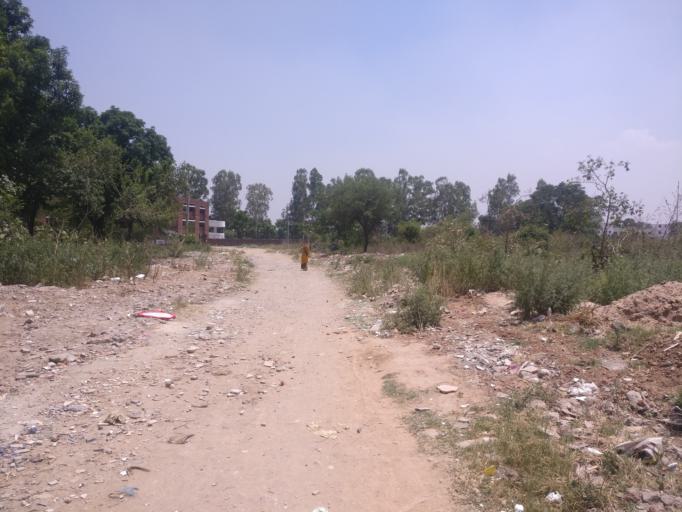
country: IN
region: Punjab
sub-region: Ajitgarh
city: Mohali
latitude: 30.7289
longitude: 76.7286
